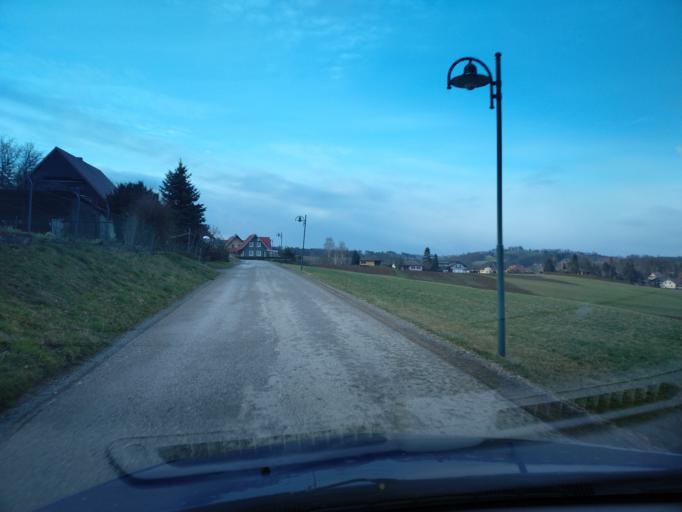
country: AT
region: Styria
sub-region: Politischer Bezirk Deutschlandsberg
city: Pitschgau
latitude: 46.6869
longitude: 15.2641
